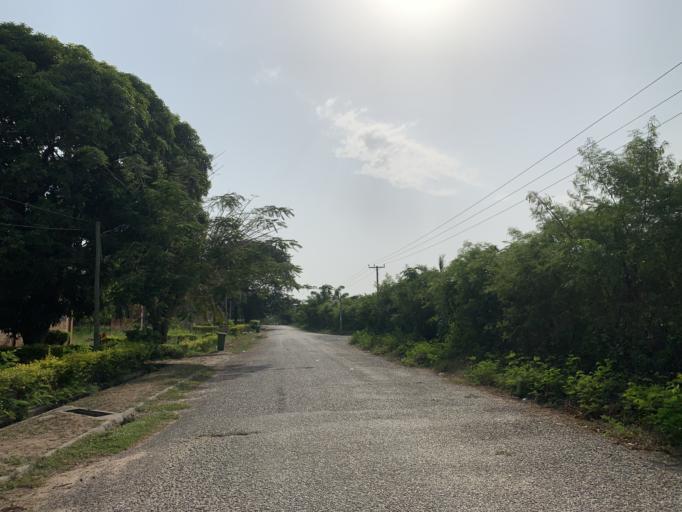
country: GH
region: Central
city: Winneba
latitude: 5.3396
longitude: -0.6280
